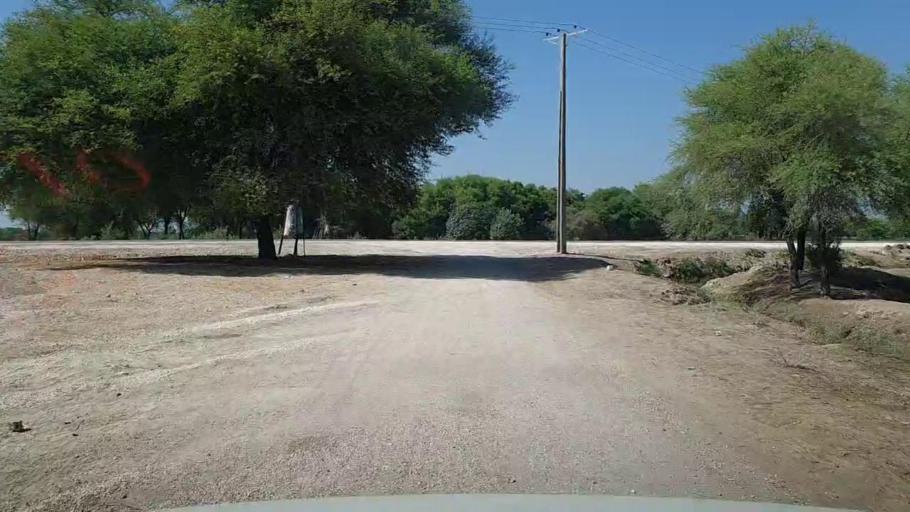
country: PK
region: Sindh
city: Kandhkot
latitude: 28.3401
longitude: 69.3623
